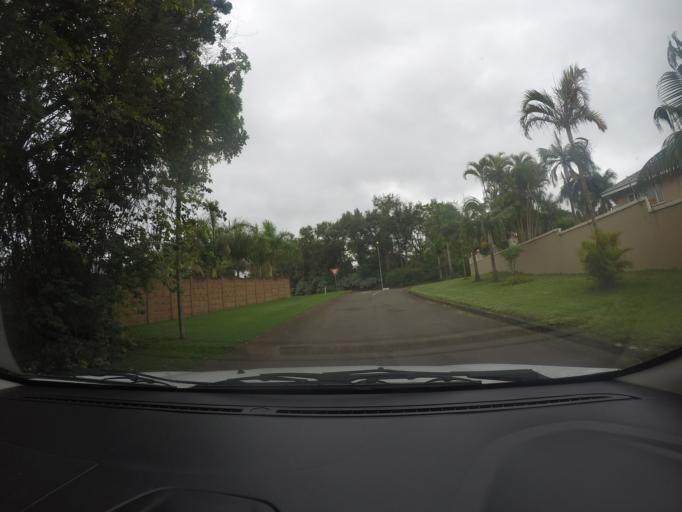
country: ZA
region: KwaZulu-Natal
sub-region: uThungulu District Municipality
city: Empangeni
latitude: -28.7617
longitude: 31.8941
